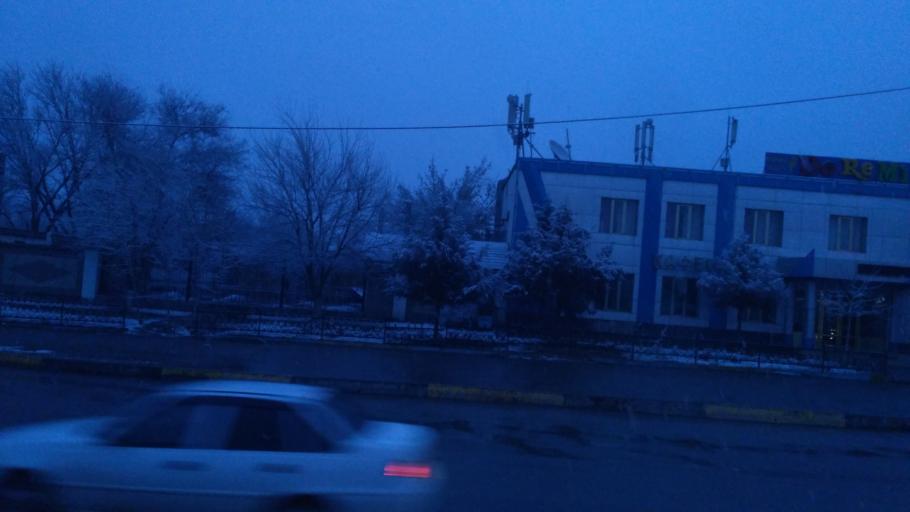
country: KZ
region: Ongtustik Qazaqstan
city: Shymkent
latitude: 42.3501
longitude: 69.5339
